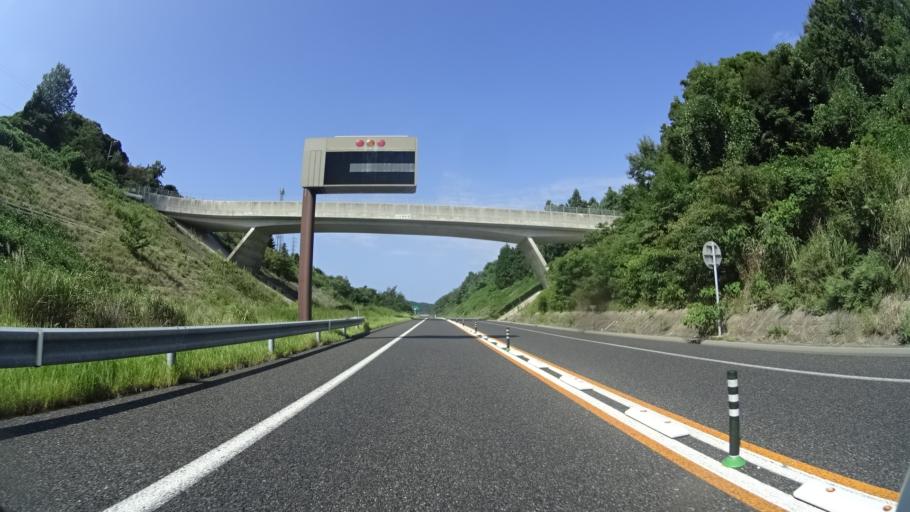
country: JP
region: Shimane
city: Gotsucho
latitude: 34.9715
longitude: 132.1858
